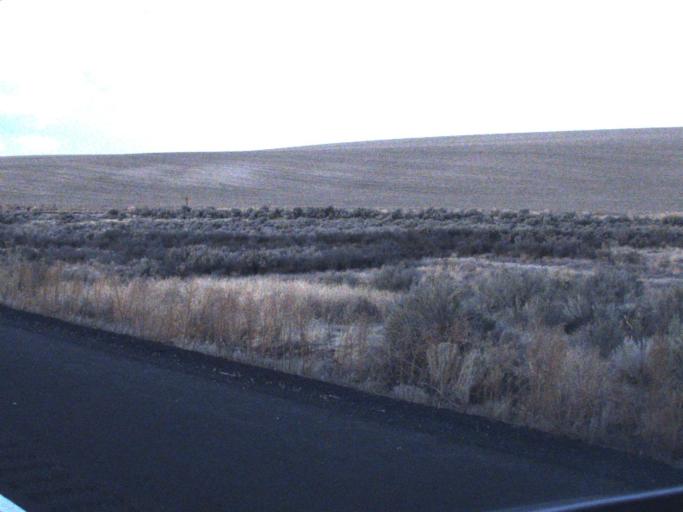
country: US
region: Washington
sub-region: Adams County
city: Ritzville
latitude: 46.9182
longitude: -118.6026
